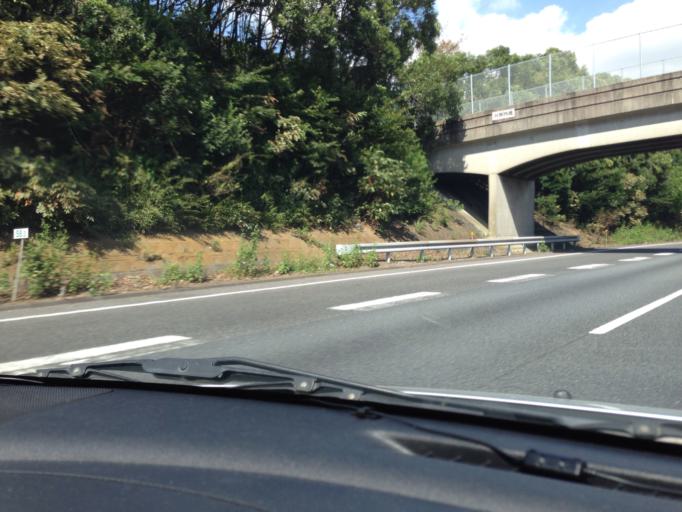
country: JP
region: Ibaraki
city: Ishioka
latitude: 36.2024
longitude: 140.2629
